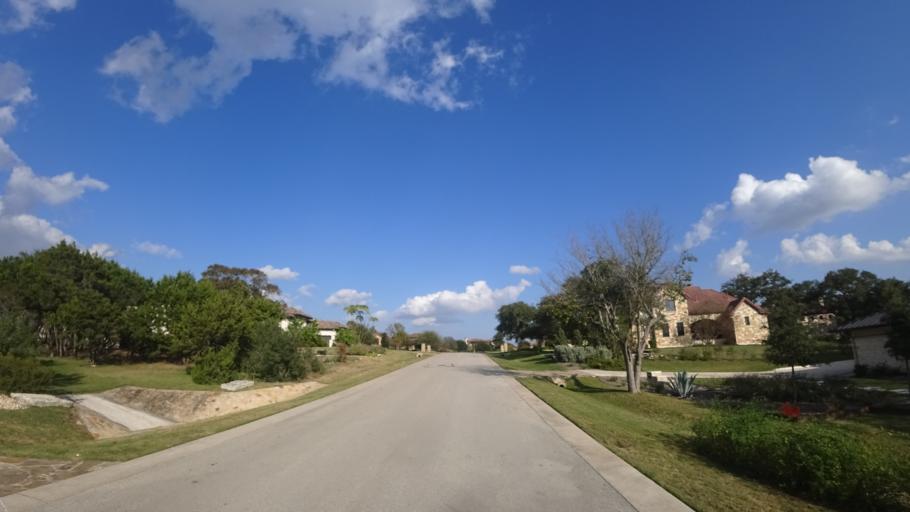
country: US
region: Texas
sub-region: Travis County
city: Barton Creek
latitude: 30.2787
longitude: -97.8781
